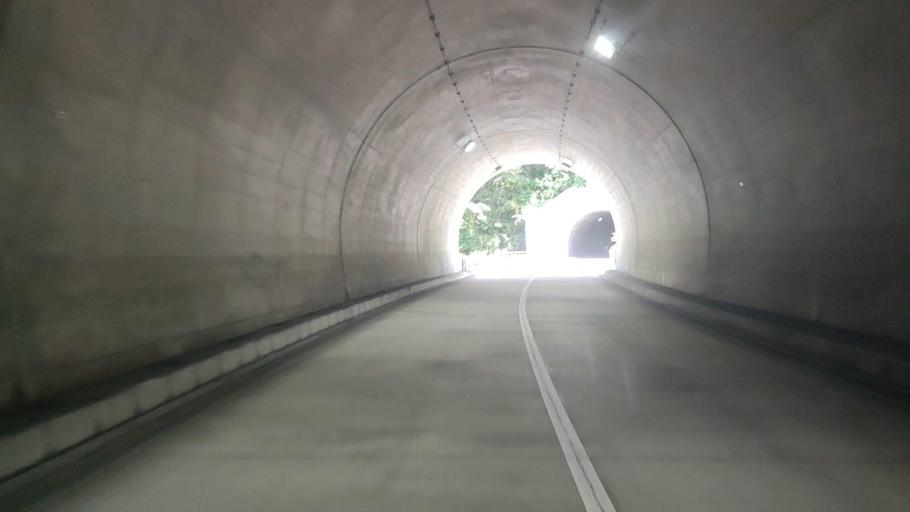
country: JP
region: Wakayama
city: Shingu
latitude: 33.8733
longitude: 135.8556
